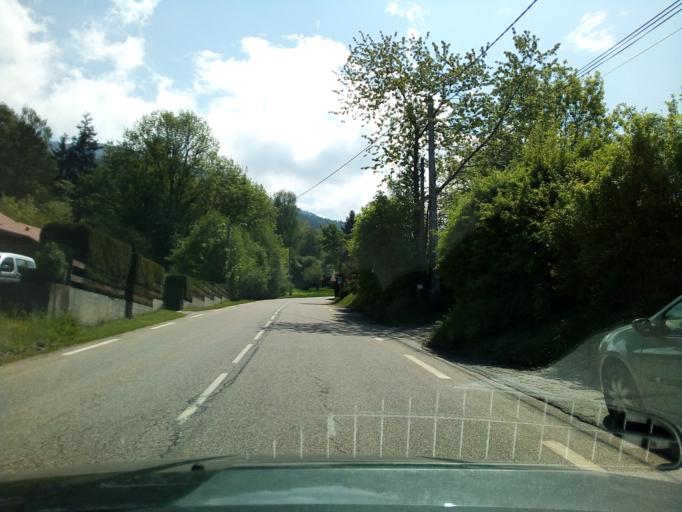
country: FR
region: Rhone-Alpes
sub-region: Departement de l'Isere
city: Revel
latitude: 45.1493
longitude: 5.8527
